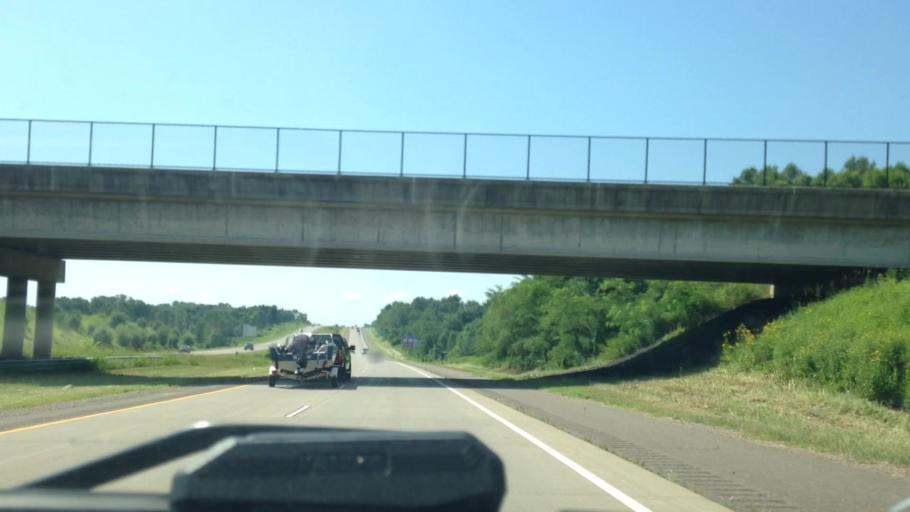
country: US
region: Wisconsin
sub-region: Barron County
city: Rice Lake
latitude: 45.4955
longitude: -91.7643
